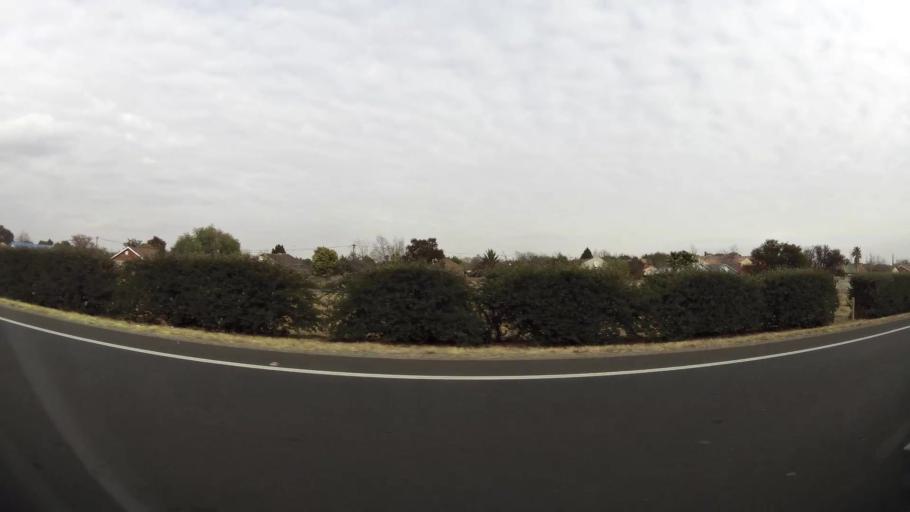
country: ZA
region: Orange Free State
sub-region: Mangaung Metropolitan Municipality
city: Bloemfontein
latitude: -29.1542
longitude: 26.1754
